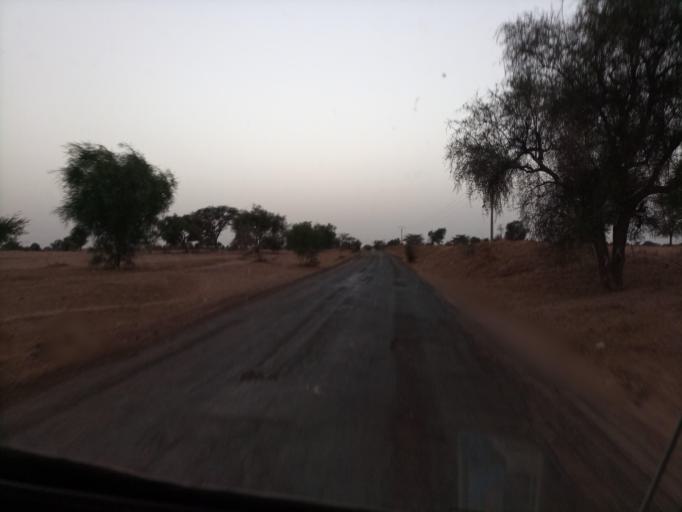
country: SN
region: Louga
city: Dara
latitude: 15.4675
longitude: -15.8398
